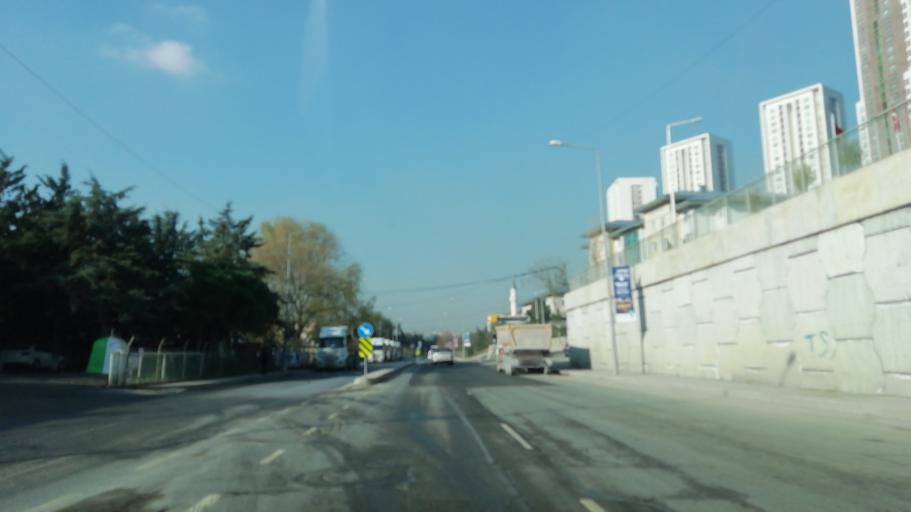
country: TR
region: Istanbul
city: Sisli
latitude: 41.0887
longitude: 28.9402
